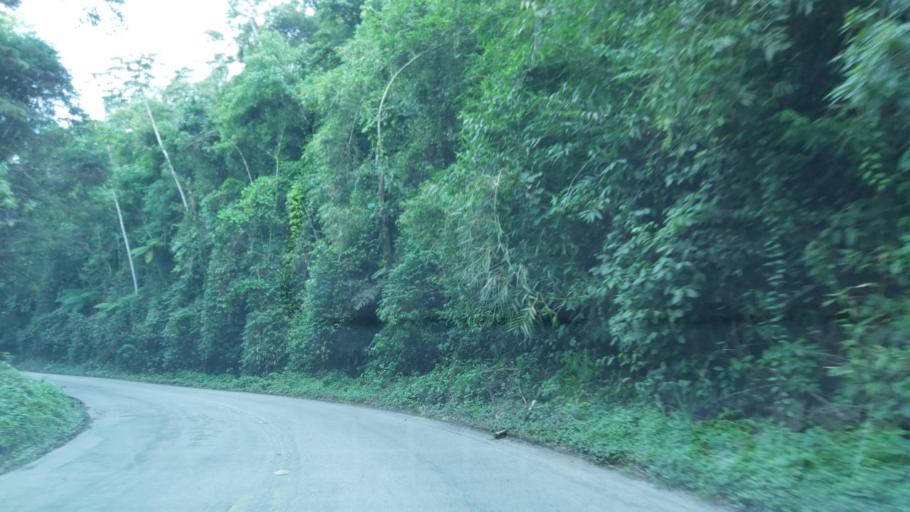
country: BR
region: Sao Paulo
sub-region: Miracatu
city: Miracatu
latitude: -24.0454
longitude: -47.5684
